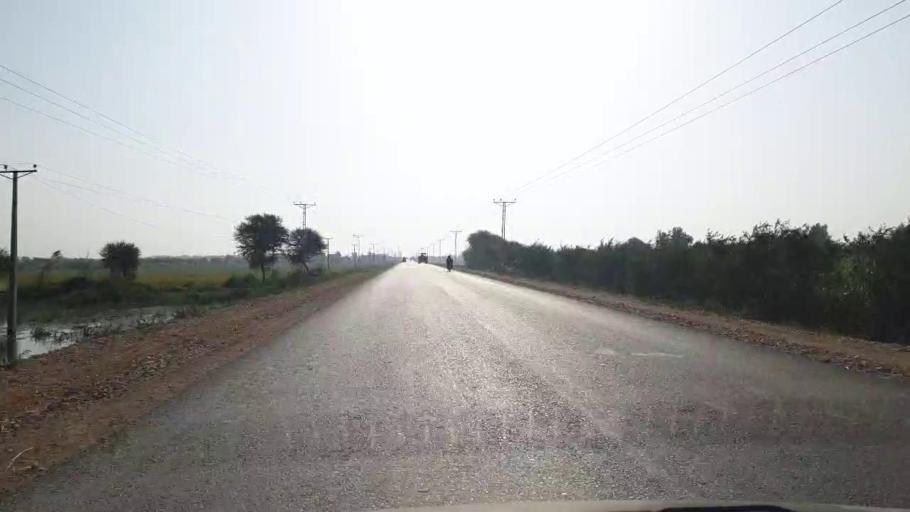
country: PK
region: Sindh
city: Badin
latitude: 24.6708
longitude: 68.8592
